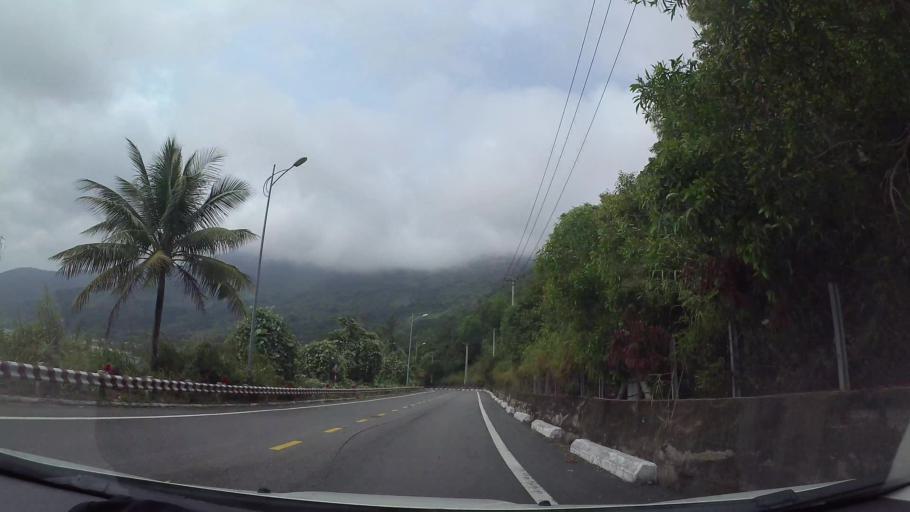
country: VN
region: Da Nang
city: Son Tra
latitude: 16.1029
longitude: 108.3021
